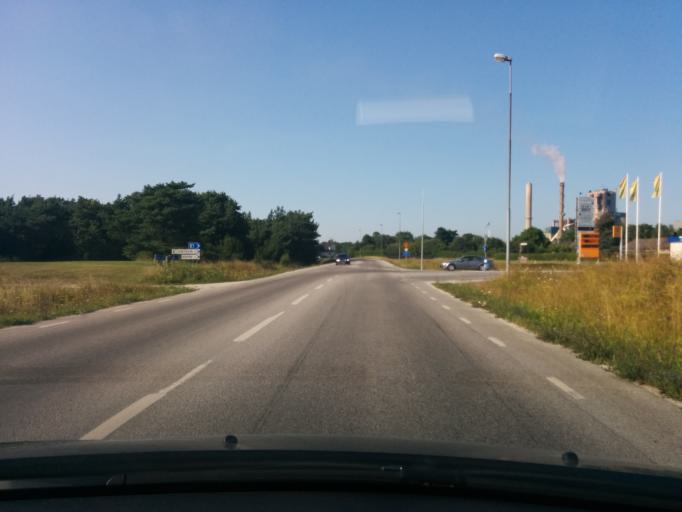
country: SE
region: Gotland
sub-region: Gotland
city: Slite
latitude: 57.7021
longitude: 18.7955
